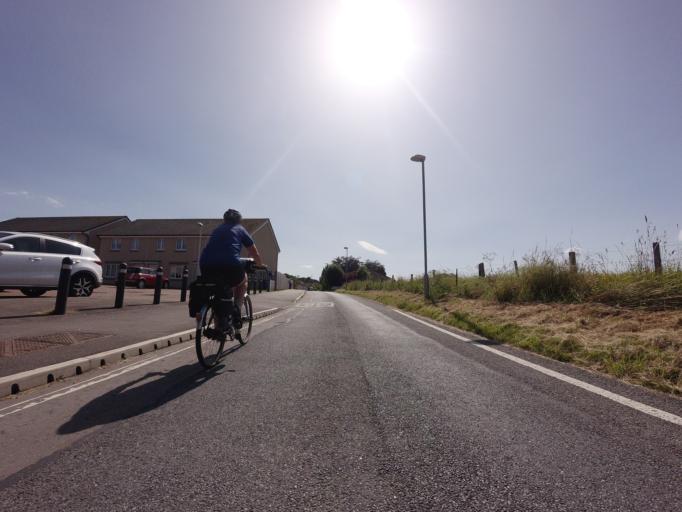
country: GB
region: Scotland
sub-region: Highland
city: Inverness
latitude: 57.4788
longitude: -4.1542
